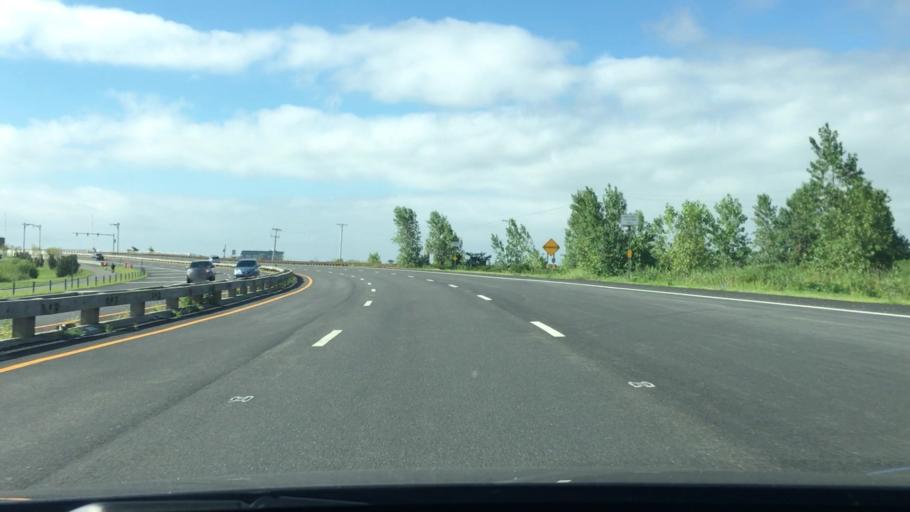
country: US
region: New York
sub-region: Nassau County
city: Seaford
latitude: 40.6179
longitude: -73.5022
